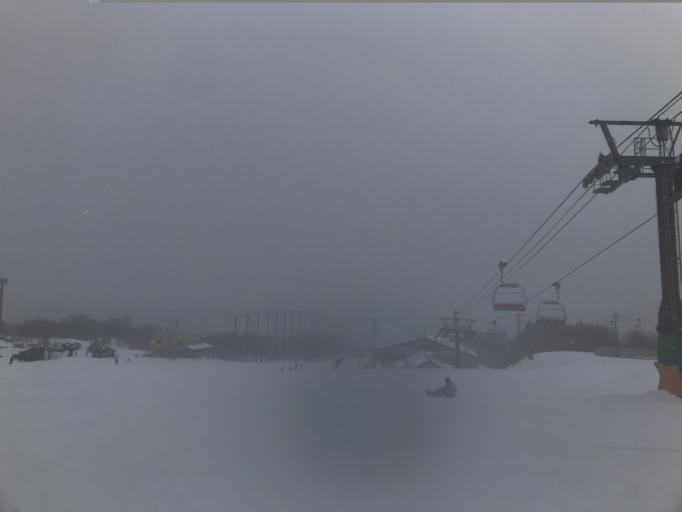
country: JP
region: Nagano
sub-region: Kitaazumi Gun
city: Hakuba
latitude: 36.7575
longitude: 137.8620
